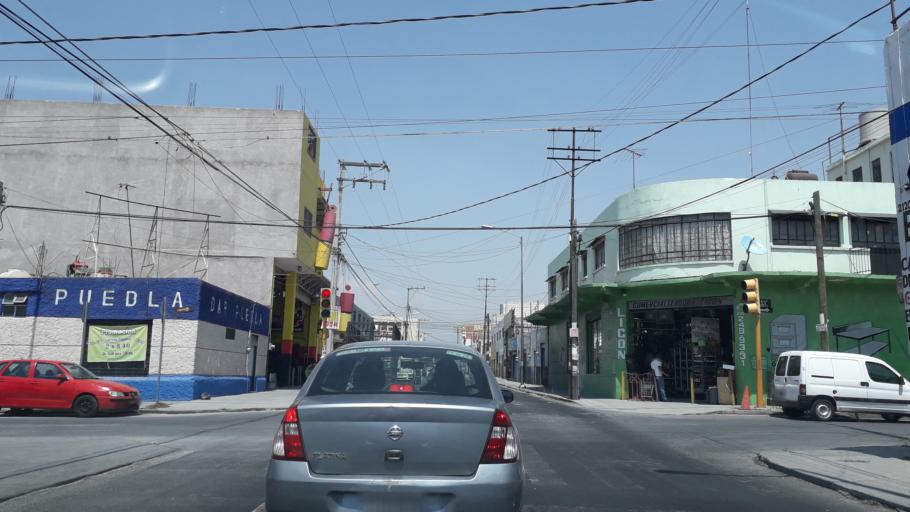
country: MX
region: Puebla
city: Puebla
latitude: 19.0537
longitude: -98.2145
